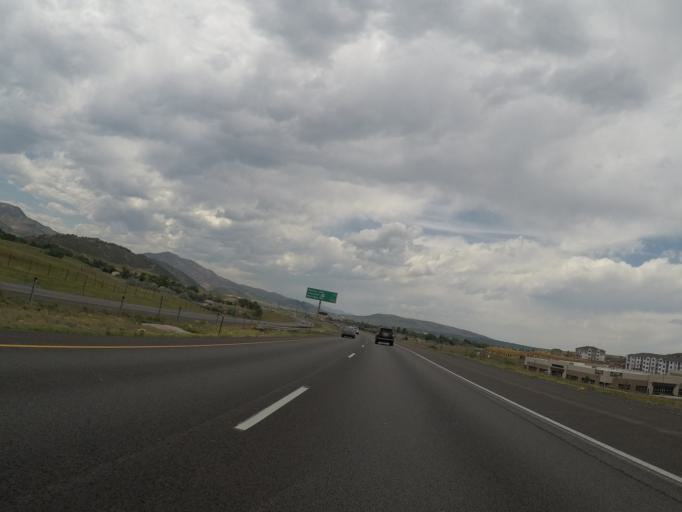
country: US
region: Colorado
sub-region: Jefferson County
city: Ken Caryl
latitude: 39.6197
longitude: -105.1502
